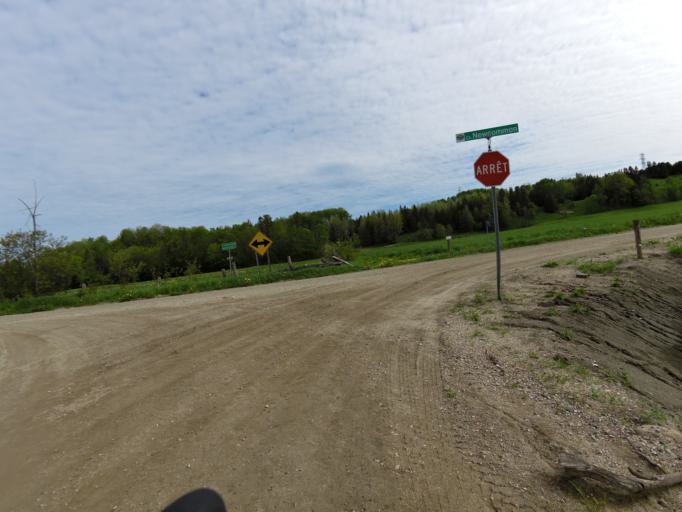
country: CA
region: Quebec
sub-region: Outaouais
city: Wakefield
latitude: 45.7291
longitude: -75.8972
